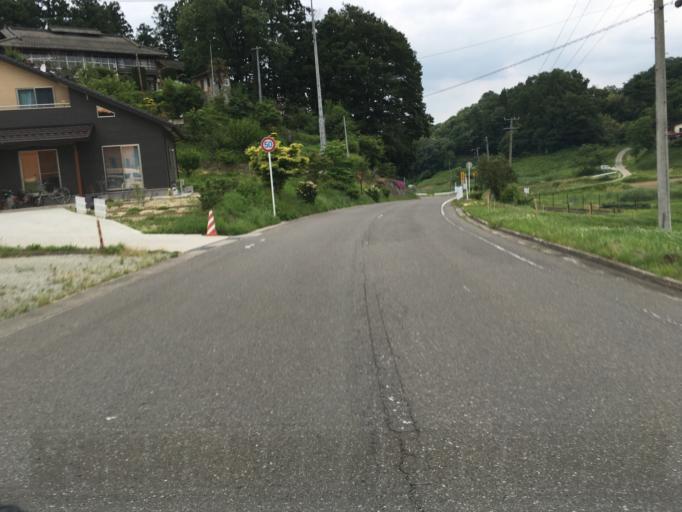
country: JP
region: Fukushima
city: Nihommatsu
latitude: 37.6317
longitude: 140.5386
